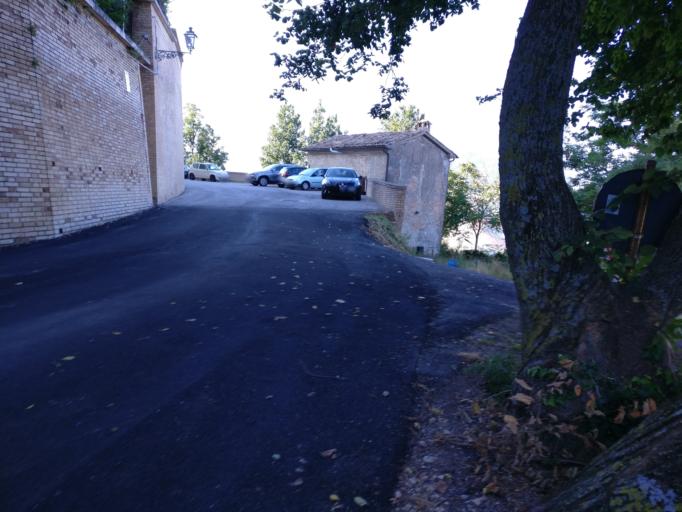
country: IT
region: The Marches
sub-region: Provincia di Ascoli Piceno
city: Montedinove
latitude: 42.9709
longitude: 13.5860
